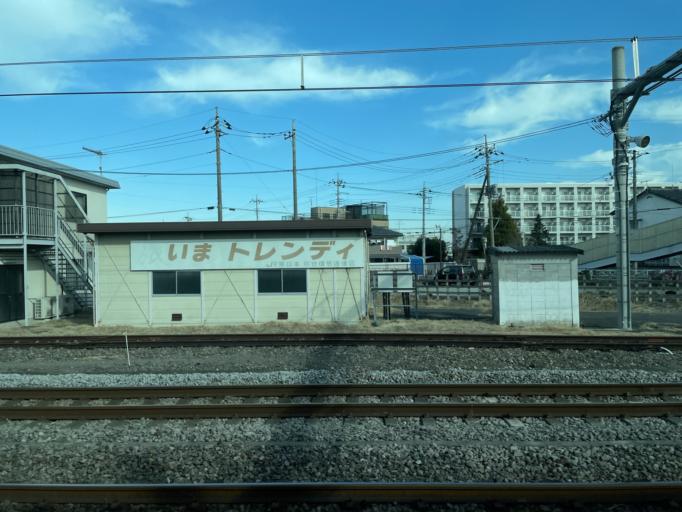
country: JP
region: Saitama
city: Honjo
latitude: 36.2353
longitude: 139.1905
